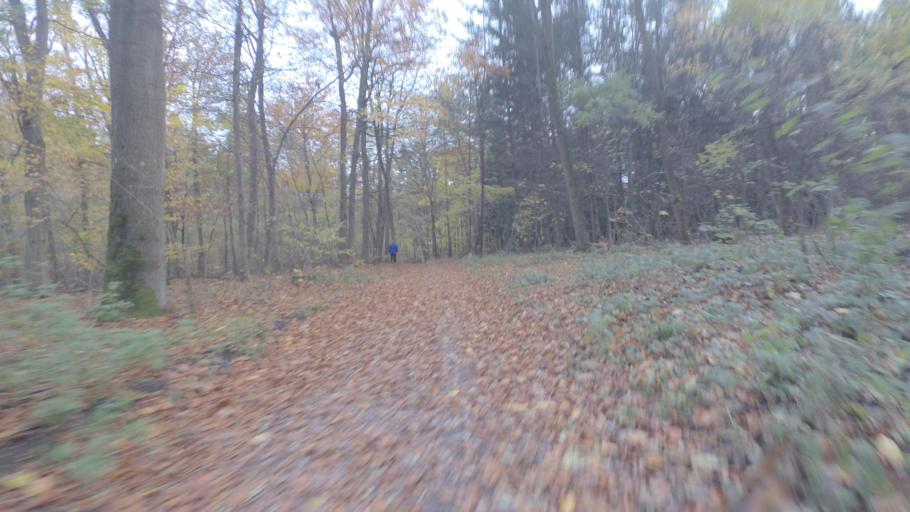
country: DE
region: Brandenburg
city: Rangsdorf
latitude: 52.3120
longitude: 13.4194
